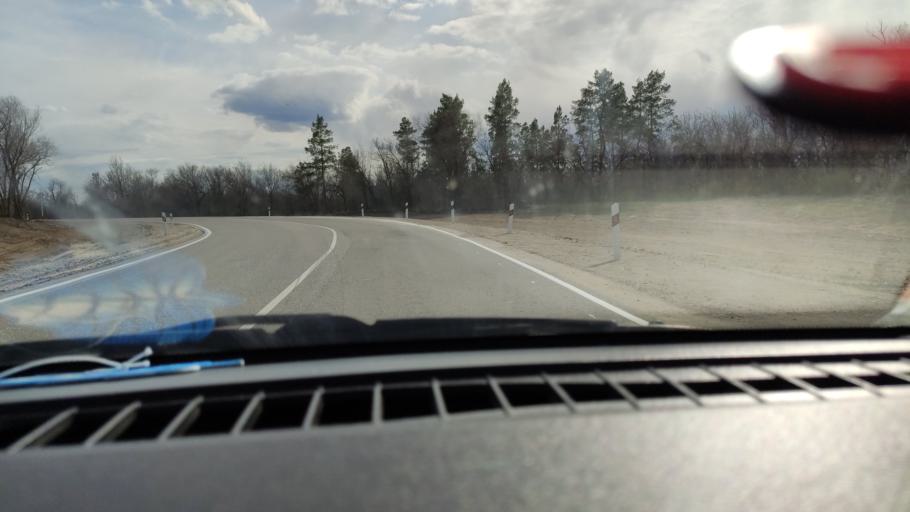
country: RU
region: Saratov
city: Krasnoarmeysk
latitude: 51.0985
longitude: 45.9544
